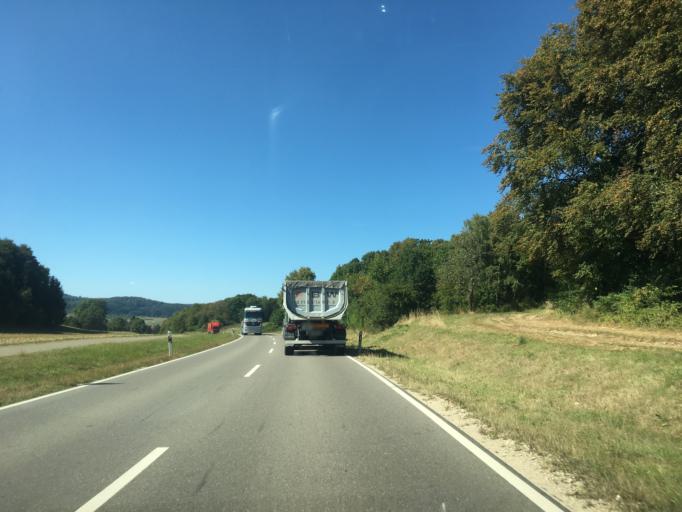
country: DE
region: Baden-Wuerttemberg
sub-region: Tuebingen Region
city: Sankt Johann
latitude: 48.3813
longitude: 9.3102
